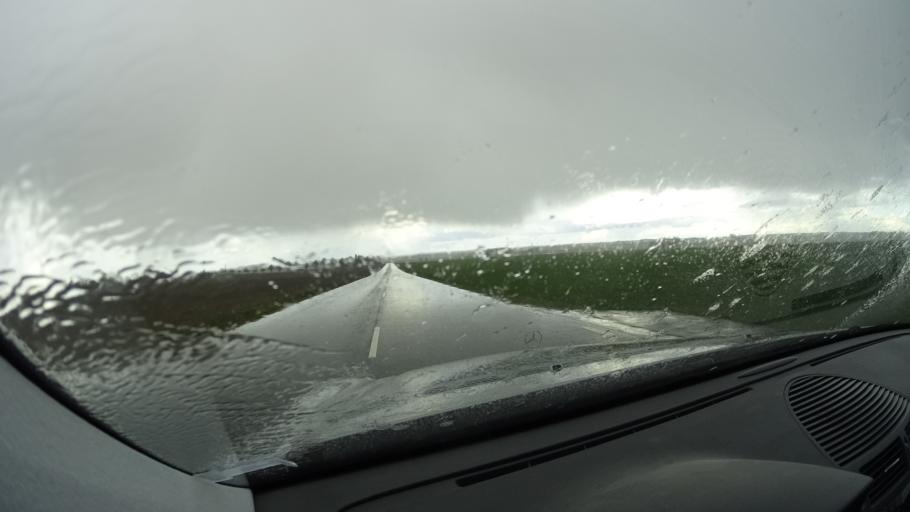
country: SE
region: Skane
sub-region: Lunds Kommun
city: Lund
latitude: 55.7613
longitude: 13.2235
